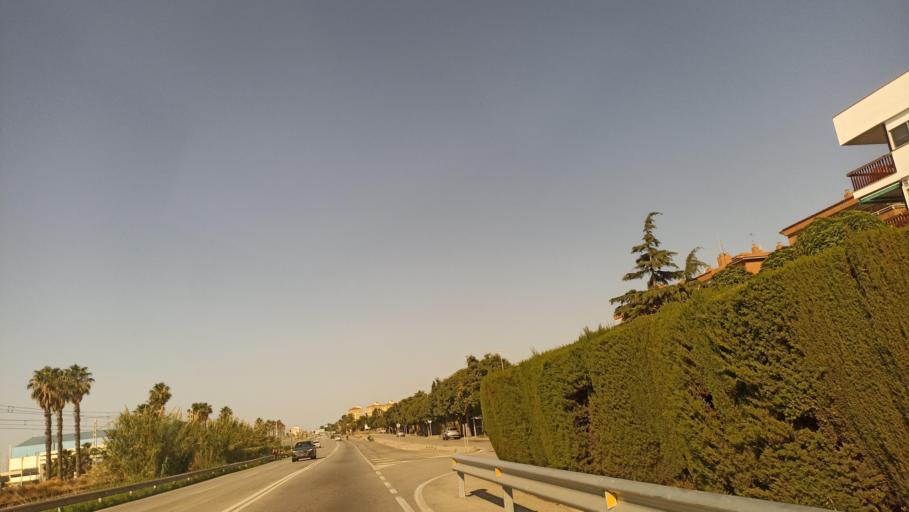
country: ES
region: Catalonia
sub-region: Provincia de Barcelona
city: Sant Andreu de Llavaneres
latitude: 41.5607
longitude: 2.5079
